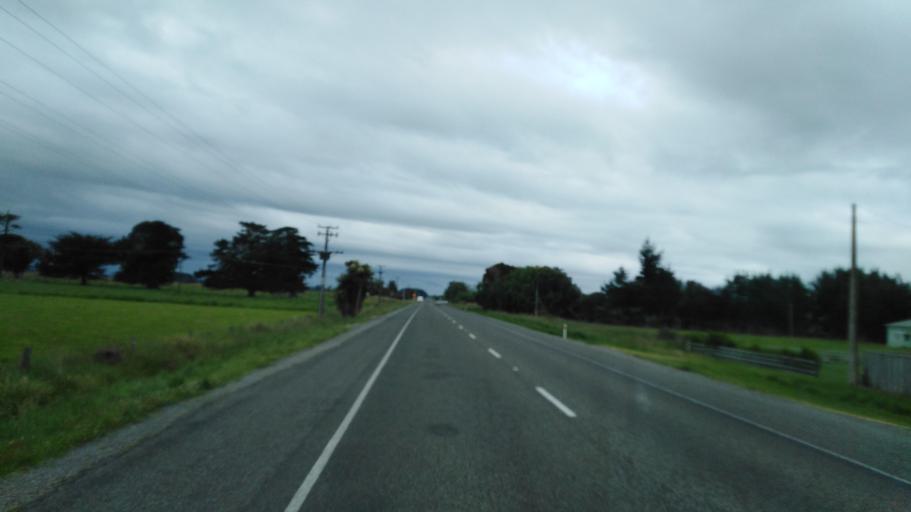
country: NZ
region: Manawatu-Wanganui
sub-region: Horowhenua District
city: Foxton
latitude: -40.3701
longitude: 175.3218
